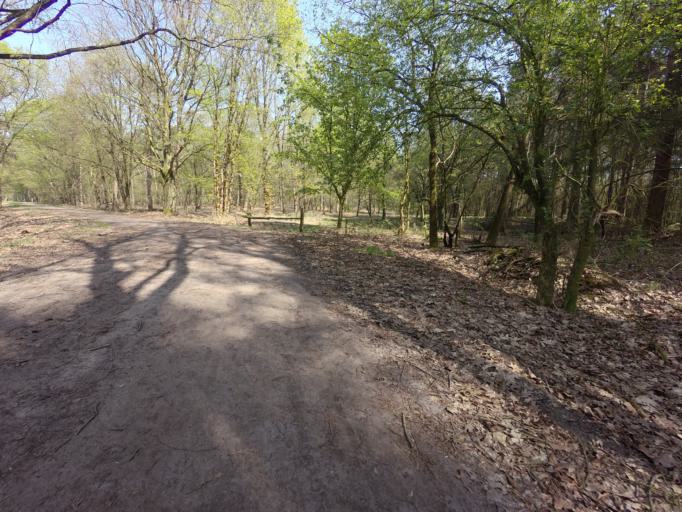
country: NL
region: North Brabant
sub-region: Gemeente Goirle
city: Goirle
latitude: 51.4982
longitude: 5.0096
